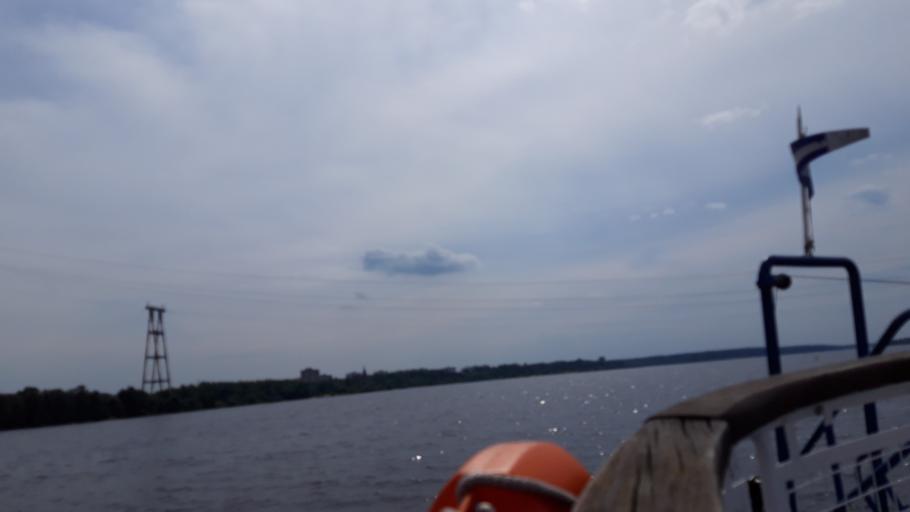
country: RU
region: Tverskaya
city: Konakovo
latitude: 56.7317
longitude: 36.7672
